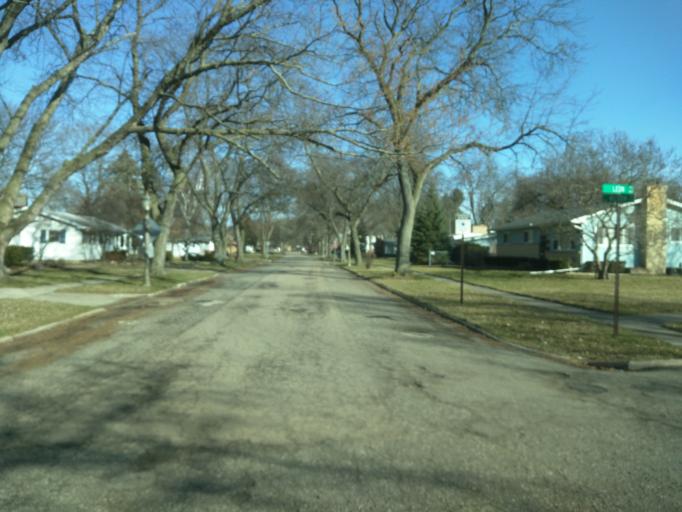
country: US
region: Michigan
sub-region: Ingham County
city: Edgemont Park
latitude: 42.7650
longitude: -84.5881
